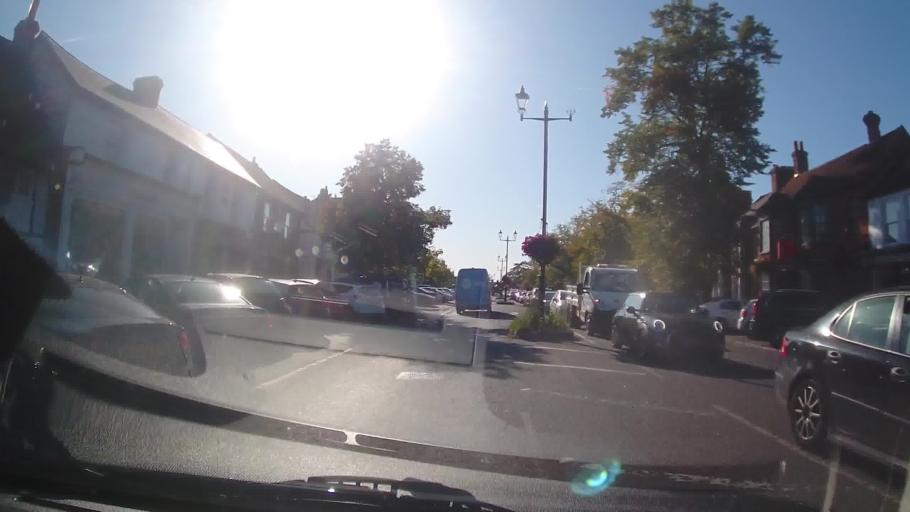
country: GB
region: England
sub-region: Buckinghamshire
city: Beaconsfield
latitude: 51.6019
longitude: -0.6344
